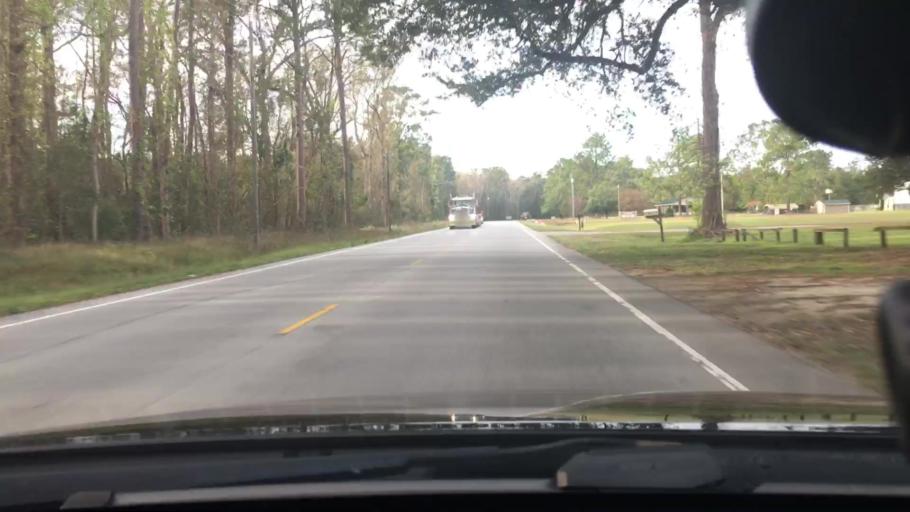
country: US
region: North Carolina
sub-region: Craven County
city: Vanceboro
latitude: 35.2261
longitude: -77.0701
